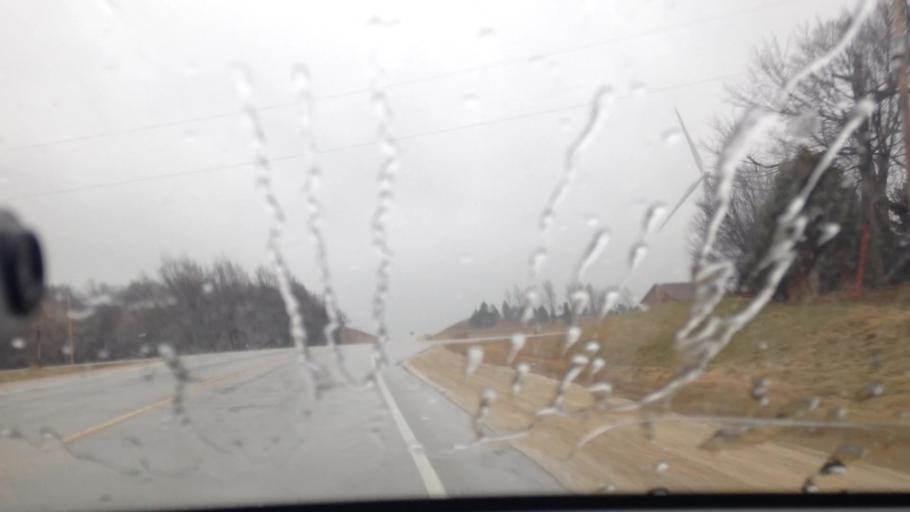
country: US
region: Wisconsin
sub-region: Dodge County
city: Theresa
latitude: 43.4394
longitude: -88.4808
